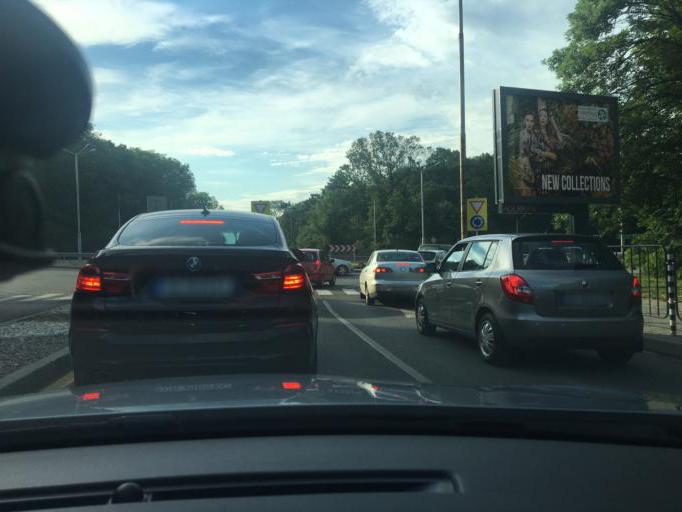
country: BG
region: Sofia-Capital
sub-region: Stolichna Obshtina
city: Sofia
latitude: 42.6771
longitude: 23.3422
